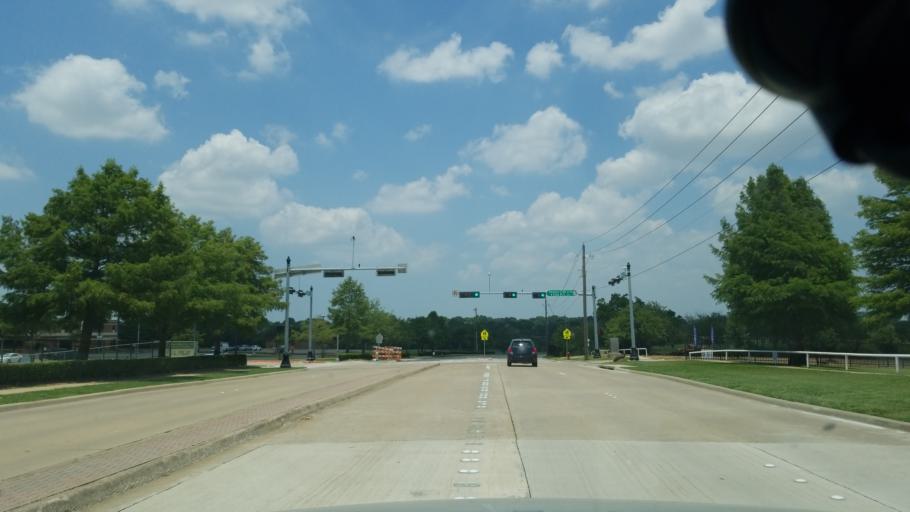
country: US
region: Texas
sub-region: Dallas County
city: Carrollton
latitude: 32.9639
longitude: -96.8776
